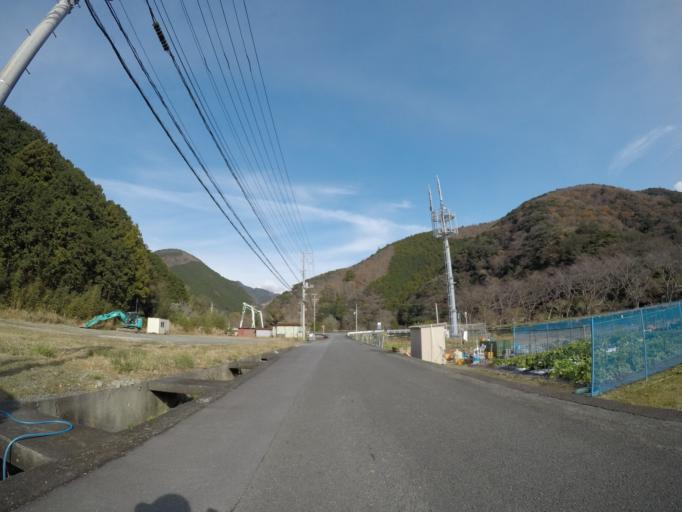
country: JP
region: Shizuoka
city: Heda
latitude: 34.7869
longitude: 138.8006
